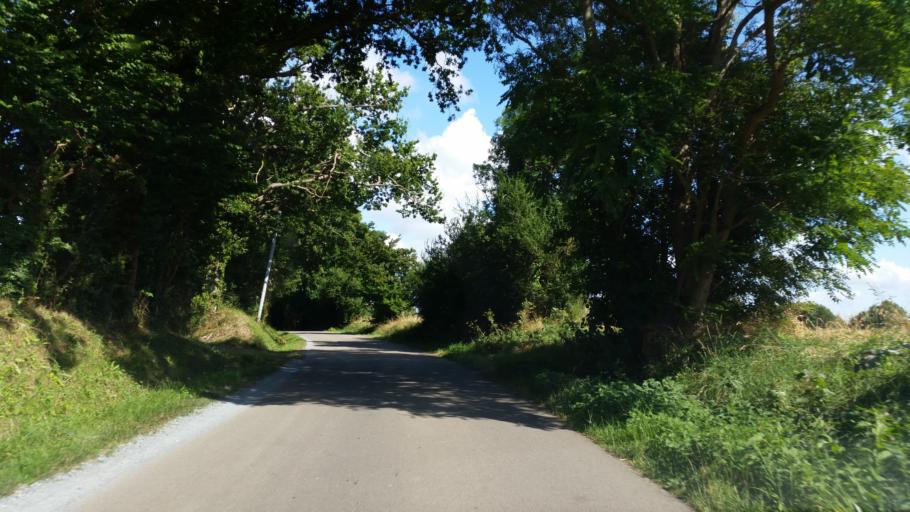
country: FR
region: Lower Normandy
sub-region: Departement du Calvados
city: Amfreville
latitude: 49.2478
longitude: -0.2244
